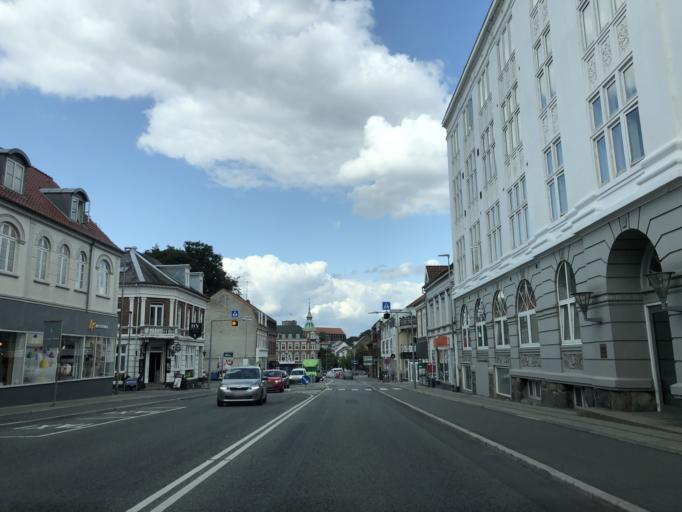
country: DK
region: South Denmark
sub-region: Kolding Kommune
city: Kolding
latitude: 55.4850
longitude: 9.4718
